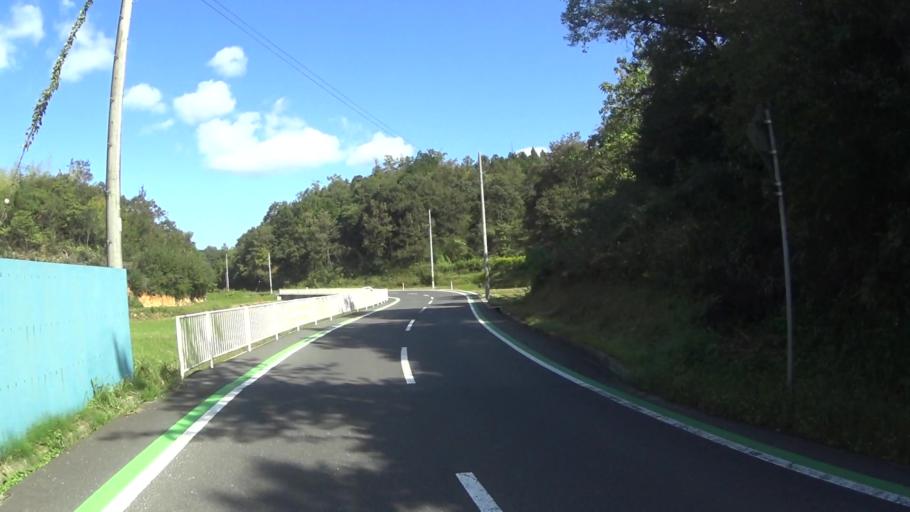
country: JP
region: Kyoto
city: Miyazu
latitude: 35.6367
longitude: 135.0702
